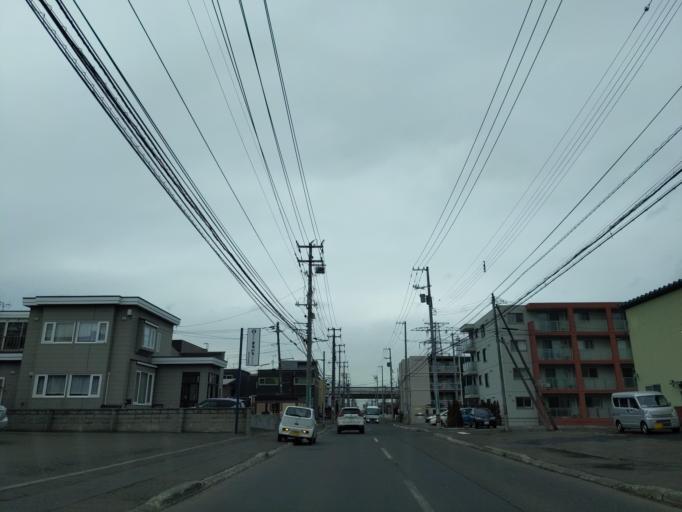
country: JP
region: Hokkaido
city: Sapporo
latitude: 43.0917
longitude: 141.4012
